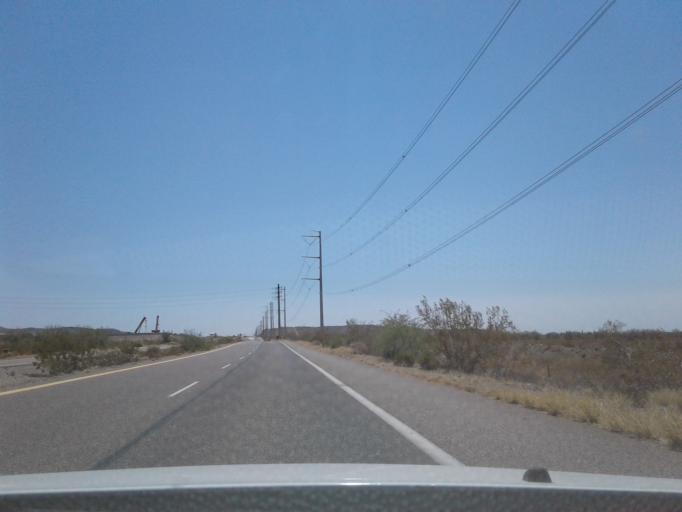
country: US
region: Arizona
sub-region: Maricopa County
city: Laveen
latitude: 33.2909
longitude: -112.1028
